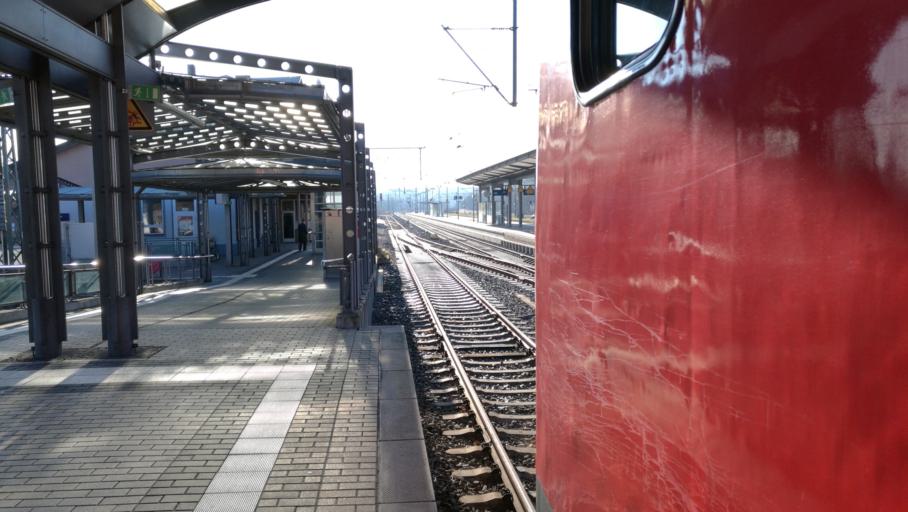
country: DE
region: Bavaria
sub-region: Regierungsbezirk Mittelfranken
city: Roth
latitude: 49.2417
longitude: 11.0829
